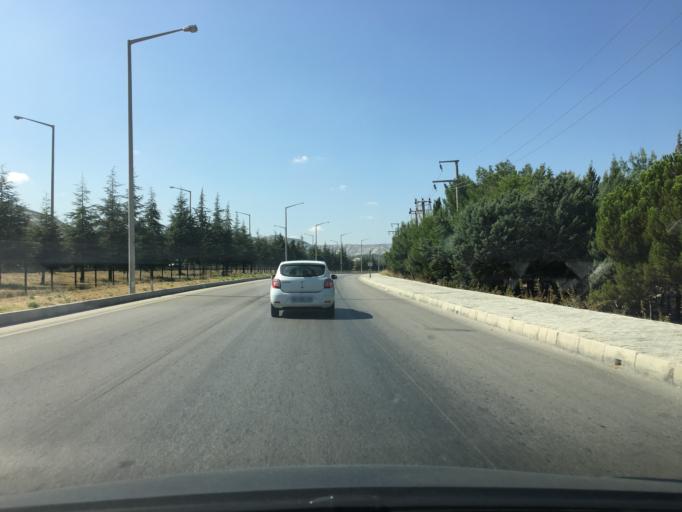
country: TR
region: Burdur
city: Burdur
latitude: 37.7340
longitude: 30.3097
